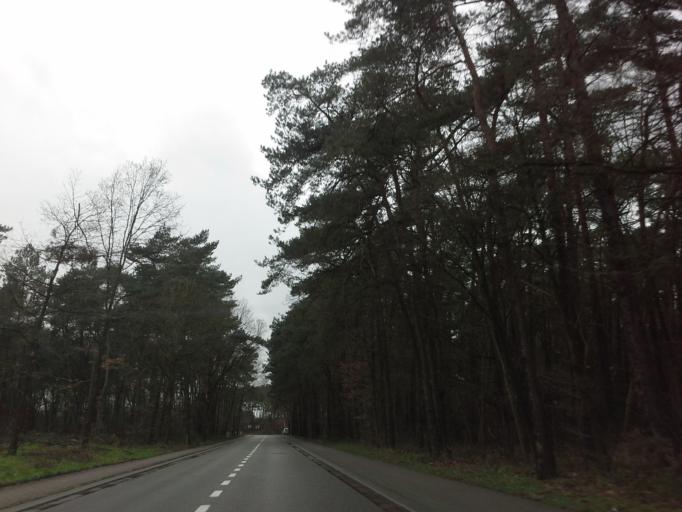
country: BE
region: Flanders
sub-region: Provincie Antwerpen
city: Meerhout
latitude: 51.1424
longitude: 5.0986
